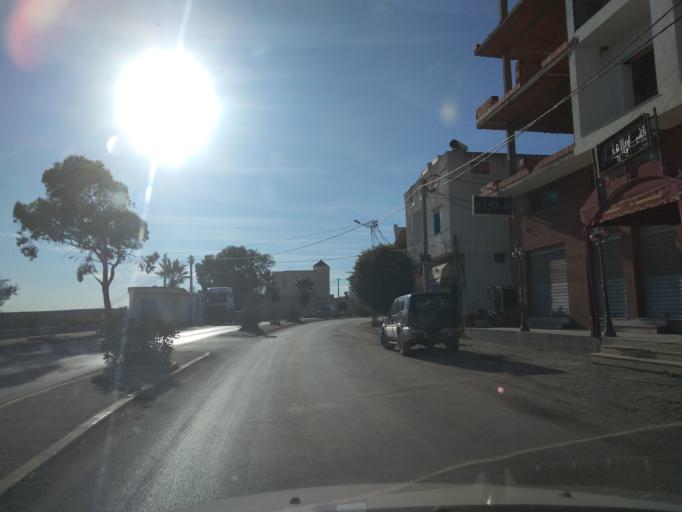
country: TN
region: Ariana
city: Qal'at al Andalus
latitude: 37.0571
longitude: 10.1080
